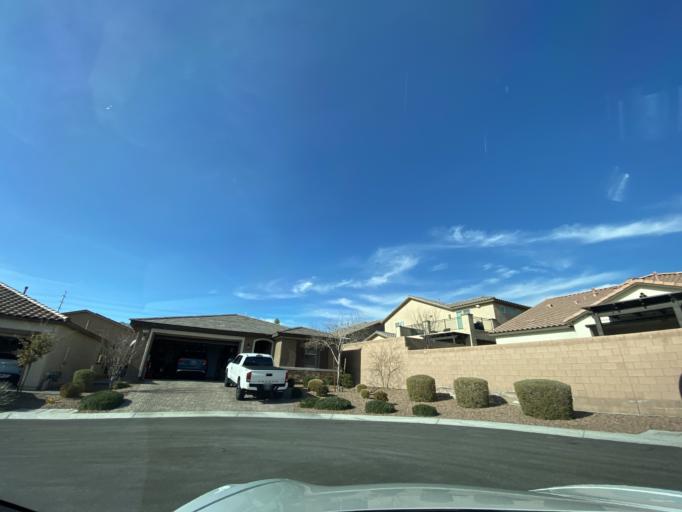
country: US
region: Nevada
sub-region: Clark County
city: Summerlin South
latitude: 36.2918
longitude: -115.3307
